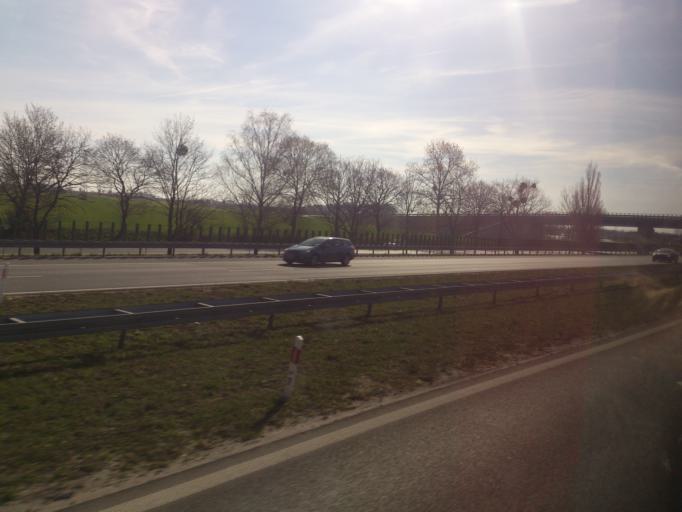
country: PL
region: Kujawsko-Pomorskie
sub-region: Powiat aleksandrowski
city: Raciazek
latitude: 52.8470
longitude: 18.7854
